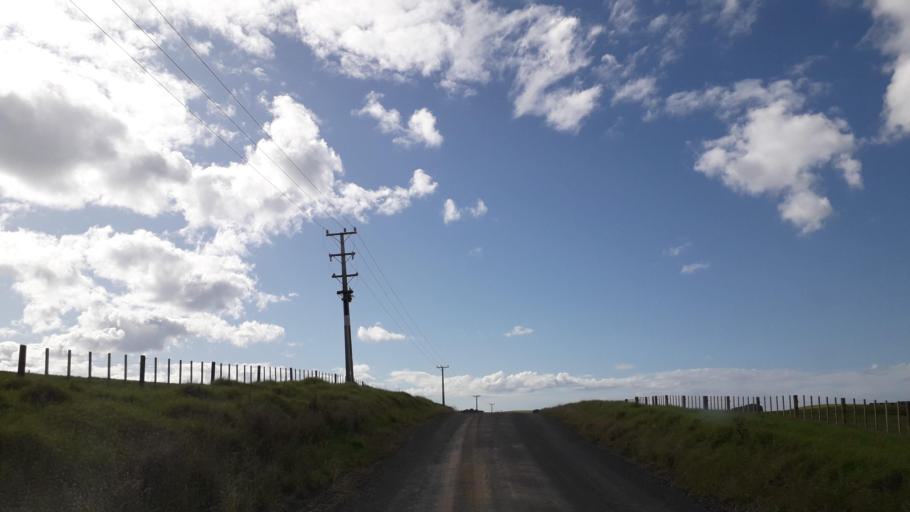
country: NZ
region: Northland
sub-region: Far North District
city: Kerikeri
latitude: -35.1461
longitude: 174.0376
